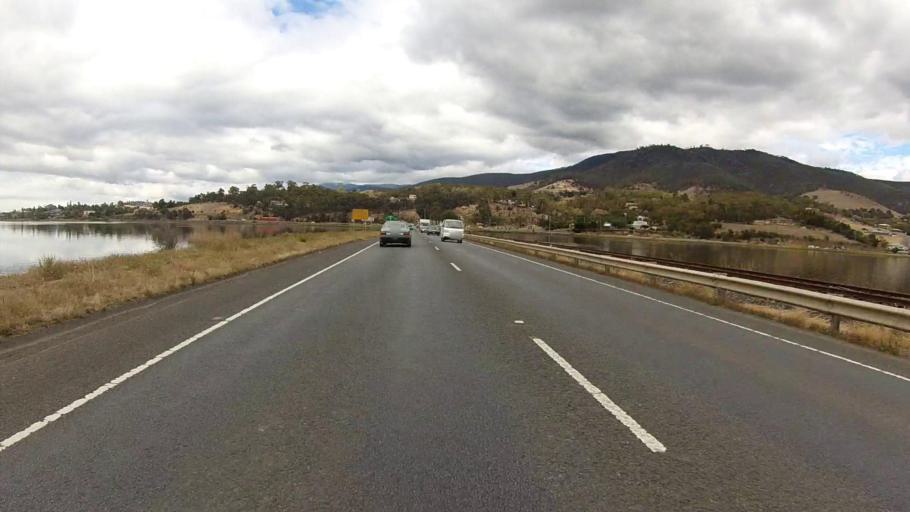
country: AU
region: Tasmania
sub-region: Glenorchy
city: Granton
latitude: -42.7454
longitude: 147.2249
